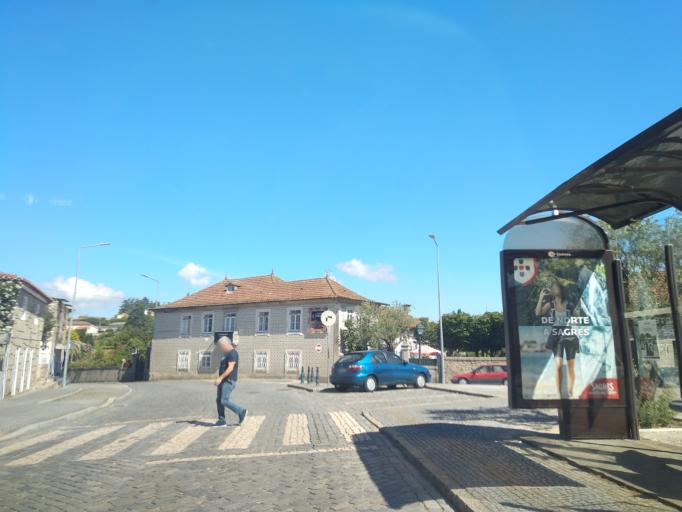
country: PT
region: Porto
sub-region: Pacos de Ferreira
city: Freamunde
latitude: 41.2884
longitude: -8.3376
